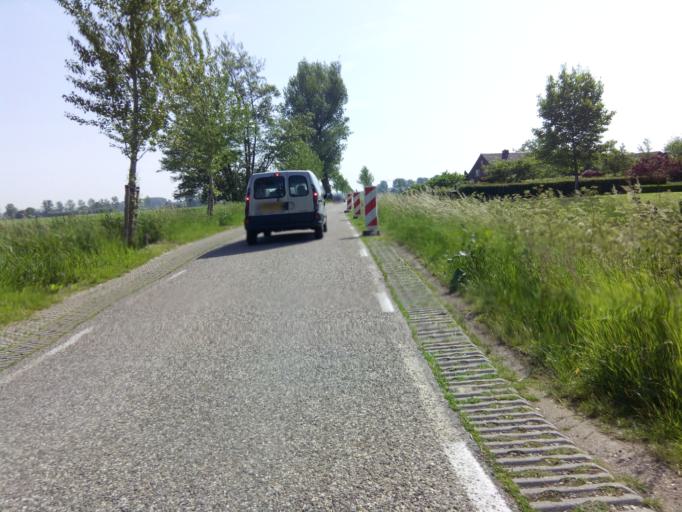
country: NL
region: Utrecht
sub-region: Gemeente Wijk bij Duurstede
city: Wijk bij Duurstede
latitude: 51.9869
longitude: 5.3851
